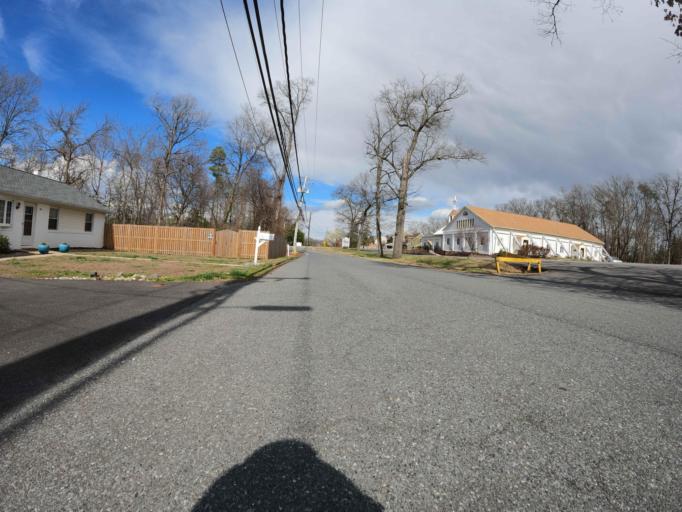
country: US
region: Maryland
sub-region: Anne Arundel County
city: Pasadena
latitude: 39.0943
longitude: -76.5733
